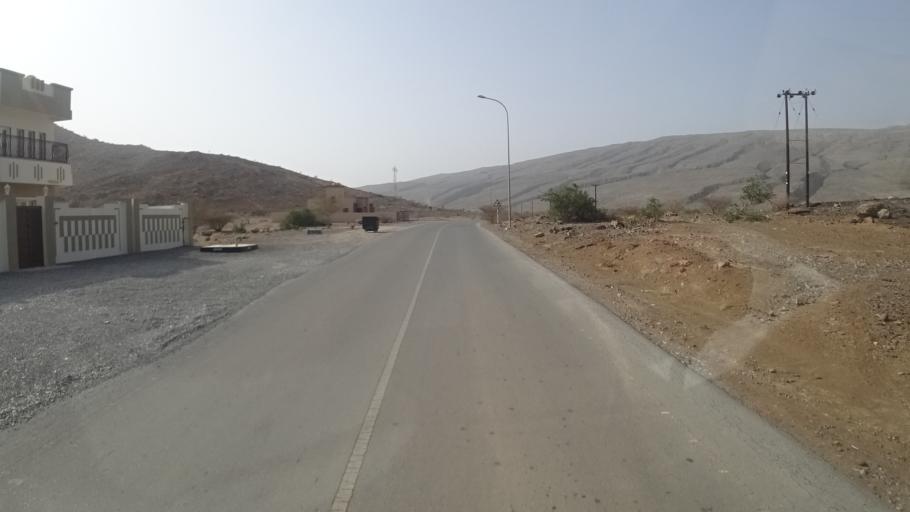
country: OM
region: Muhafazat ad Dakhiliyah
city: Bahla'
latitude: 23.0514
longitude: 57.4221
